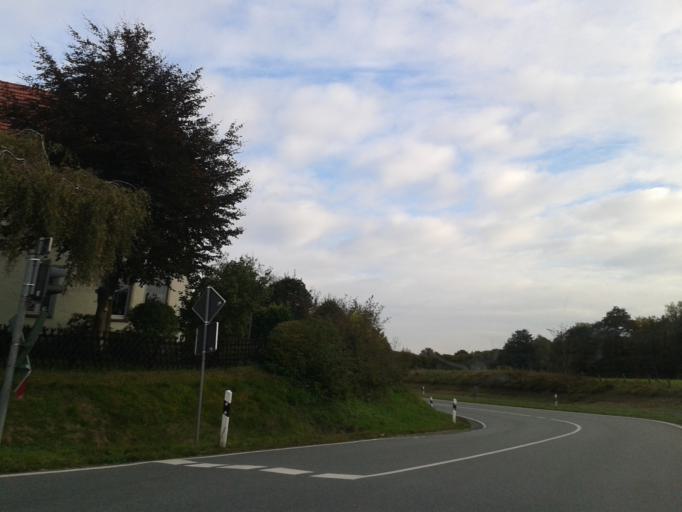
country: DE
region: North Rhine-Westphalia
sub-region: Regierungsbezirk Detmold
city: Horn
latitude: 51.8726
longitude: 8.9556
